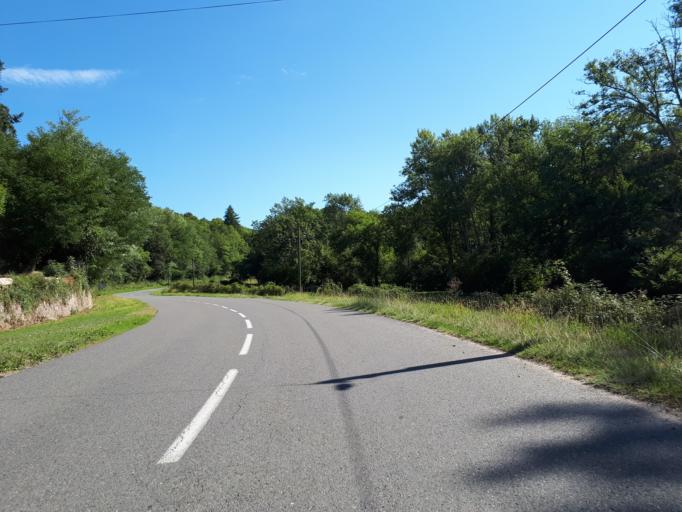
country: FR
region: Rhone-Alpes
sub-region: Departement de la Loire
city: Pouilly-les-Feurs
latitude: 45.7986
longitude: 4.2362
